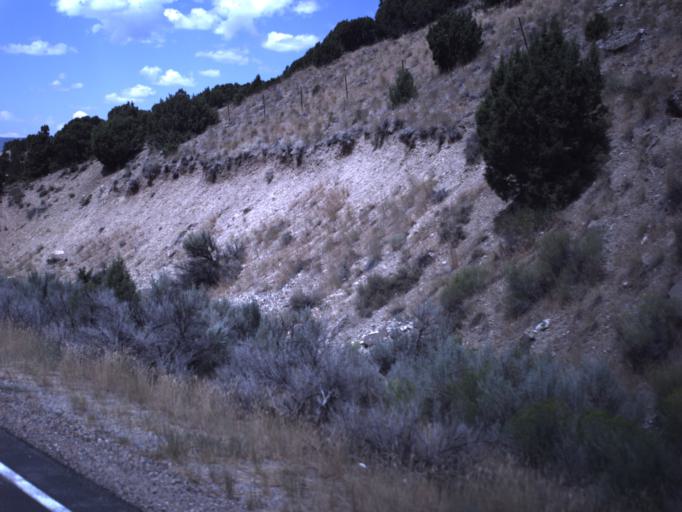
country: US
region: Utah
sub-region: Rich County
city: Randolph
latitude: 41.8244
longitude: -111.3069
